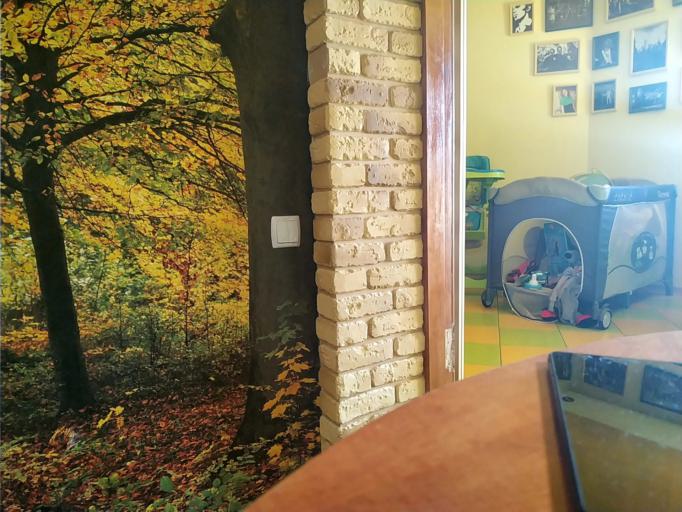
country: RU
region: Tverskaya
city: Vyshniy Volochek
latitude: 57.6004
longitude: 34.5143
